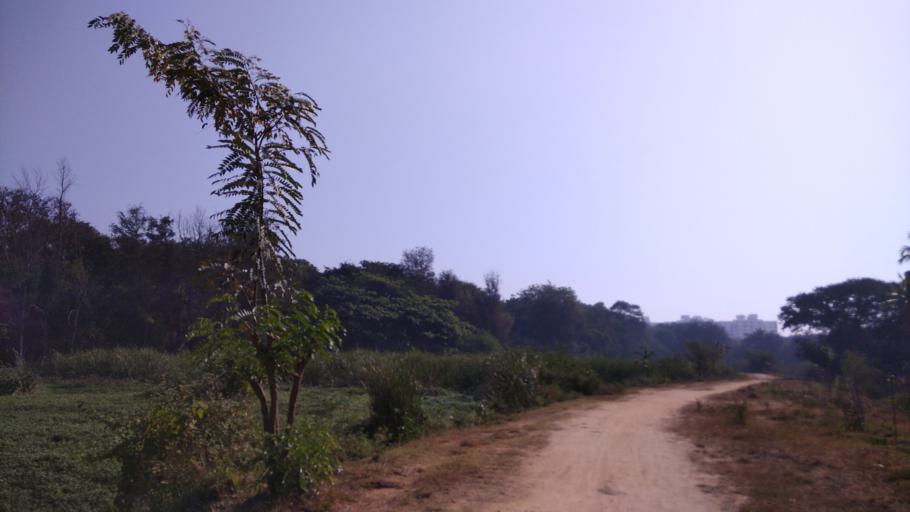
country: IN
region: Karnataka
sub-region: Bangalore Rural
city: Hoskote
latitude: 12.9734
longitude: 77.7380
